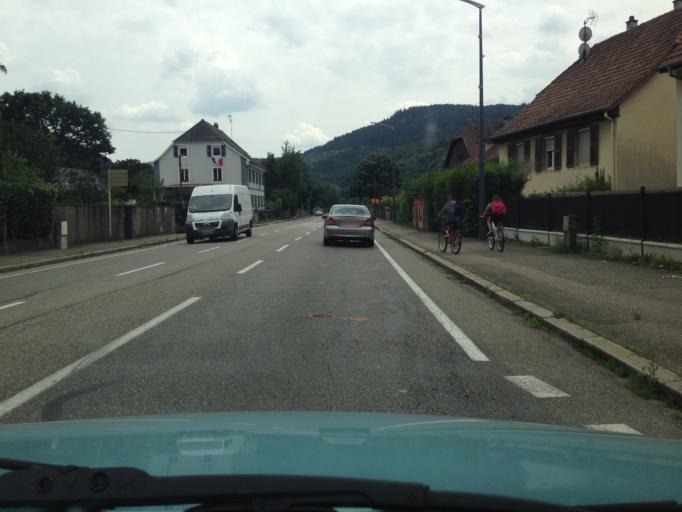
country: FR
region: Alsace
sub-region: Departement du Haut-Rhin
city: Bitschwiller-les-Thann
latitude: 47.8272
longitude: 7.0809
